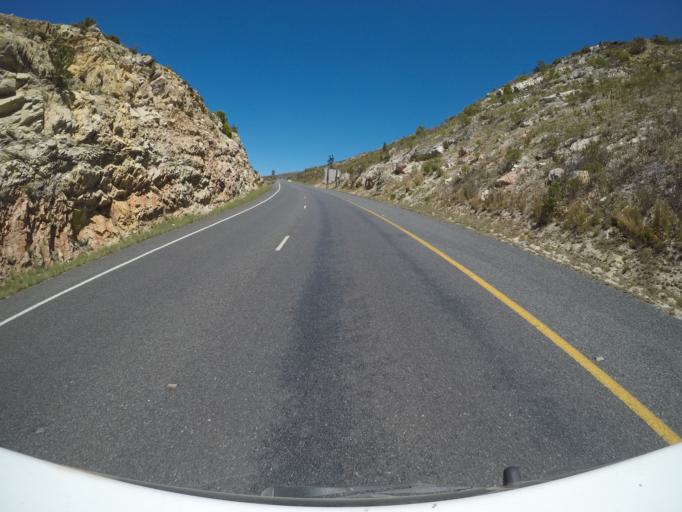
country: ZA
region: Western Cape
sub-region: Overberg District Municipality
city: Grabouw
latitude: -34.2180
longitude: 19.1870
